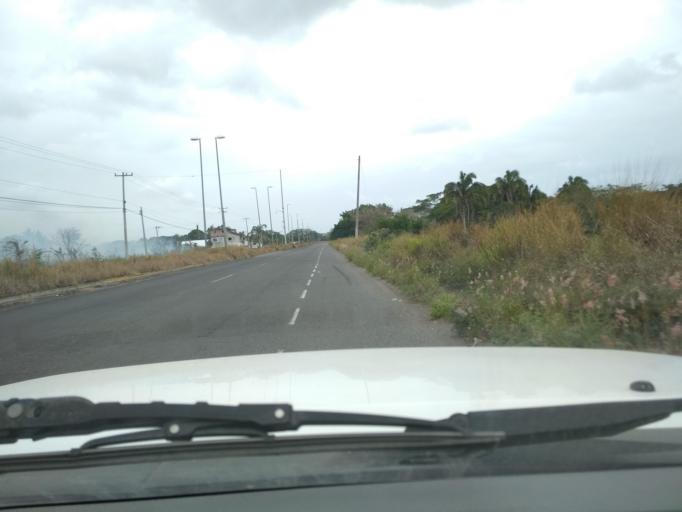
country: MX
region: Veracruz
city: Paso del Toro
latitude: 19.0630
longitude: -96.1316
